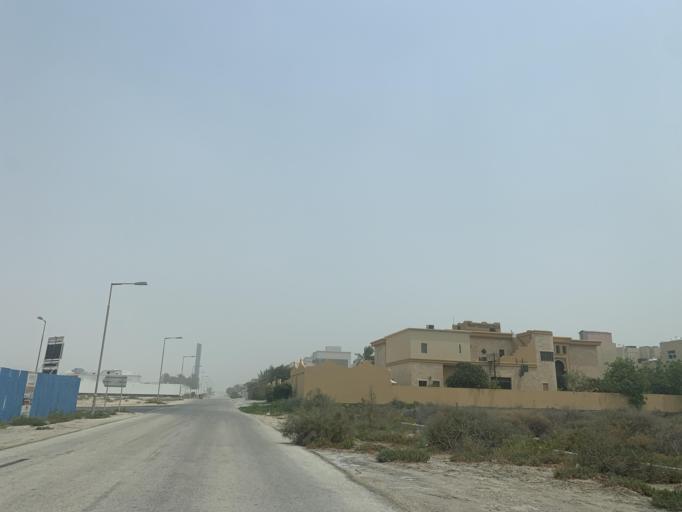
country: BH
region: Central Governorate
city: Madinat Hamad
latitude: 26.1711
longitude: 50.4690
